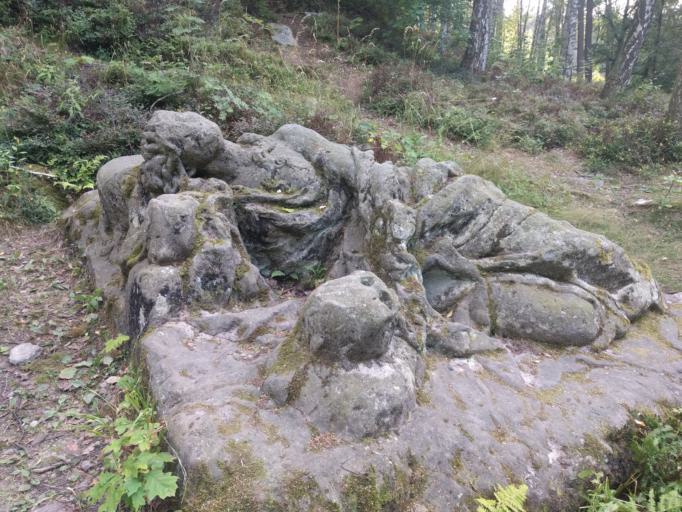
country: CZ
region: Kralovehradecky
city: Dvur Kralove nad Labem
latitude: 50.3983
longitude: 15.8508
